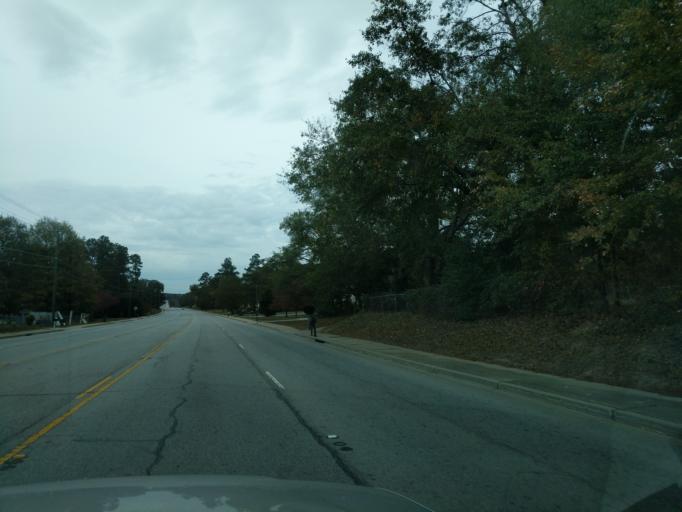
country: US
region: South Carolina
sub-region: Newberry County
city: Newberry
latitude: 34.3156
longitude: -81.6141
